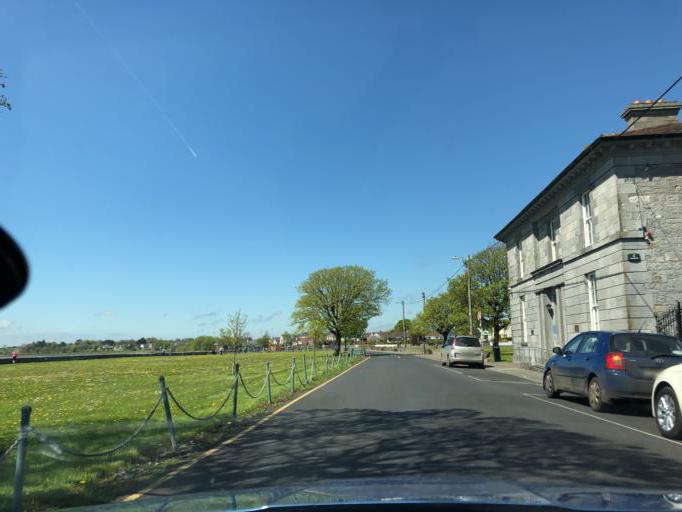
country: IE
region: Connaught
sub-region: County Galway
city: Loughrea
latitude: 53.1979
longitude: -8.5749
